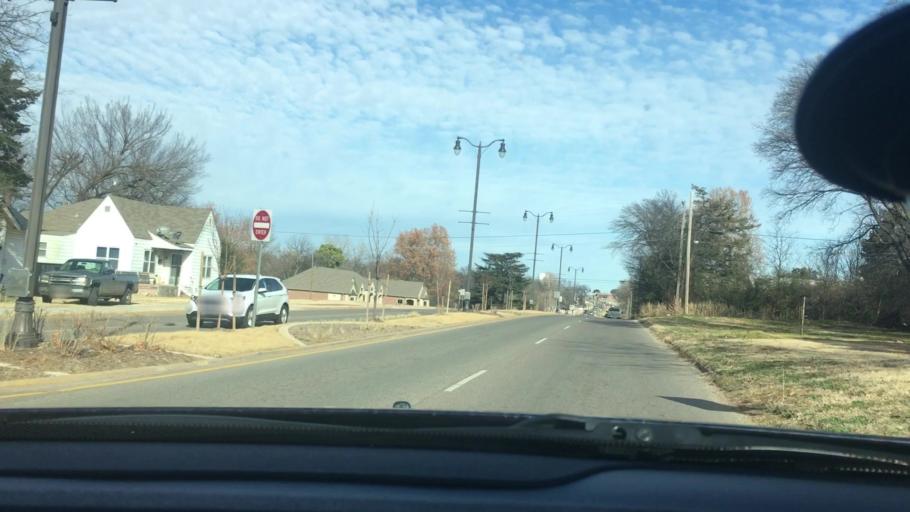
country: US
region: Oklahoma
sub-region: McClain County
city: Purcell
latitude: 35.0152
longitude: -97.3659
